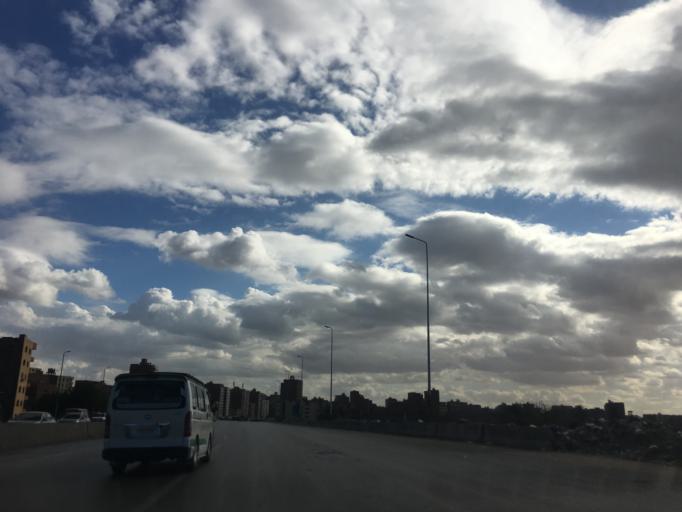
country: EG
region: Al Jizah
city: Al Jizah
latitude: 30.0257
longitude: 31.1638
